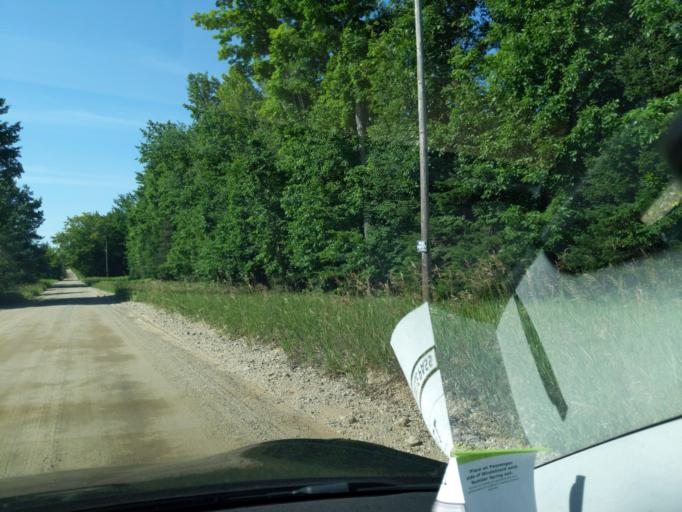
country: US
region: Michigan
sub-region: Mackinac County
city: Saint Ignace
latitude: 45.6906
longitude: -84.7127
